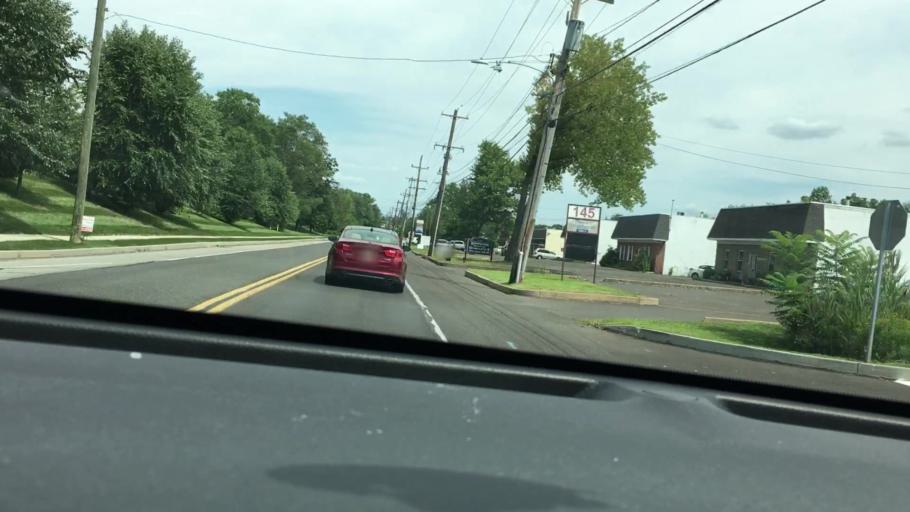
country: US
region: Pennsylvania
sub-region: Bucks County
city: Feasterville
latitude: 40.1336
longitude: -75.0050
